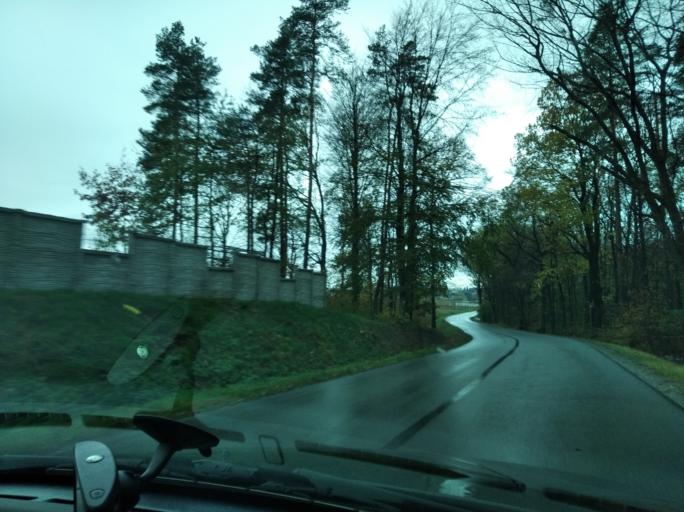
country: PL
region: Subcarpathian Voivodeship
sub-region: Powiat rzeszowski
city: Tyczyn
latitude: 49.9198
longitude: 22.0323
